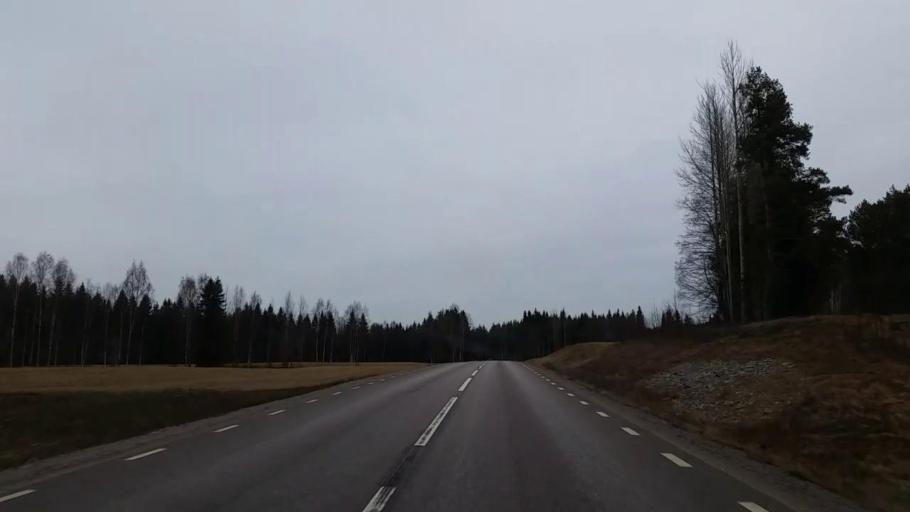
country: SE
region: Gaevleborg
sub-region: Ovanakers Kommun
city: Edsbyn
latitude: 61.1981
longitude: 15.8738
